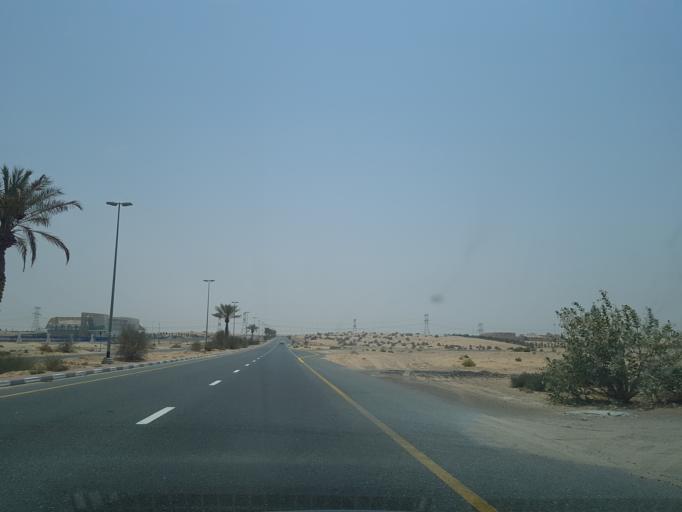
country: AE
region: Ash Shariqah
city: Sharjah
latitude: 25.1101
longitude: 55.4087
